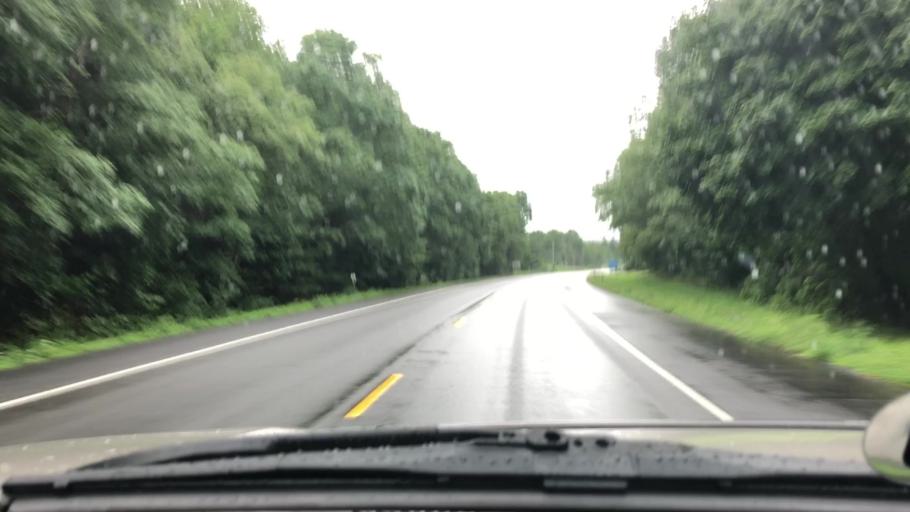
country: US
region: New York
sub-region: Greene County
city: Cairo
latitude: 42.3146
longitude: -74.0714
